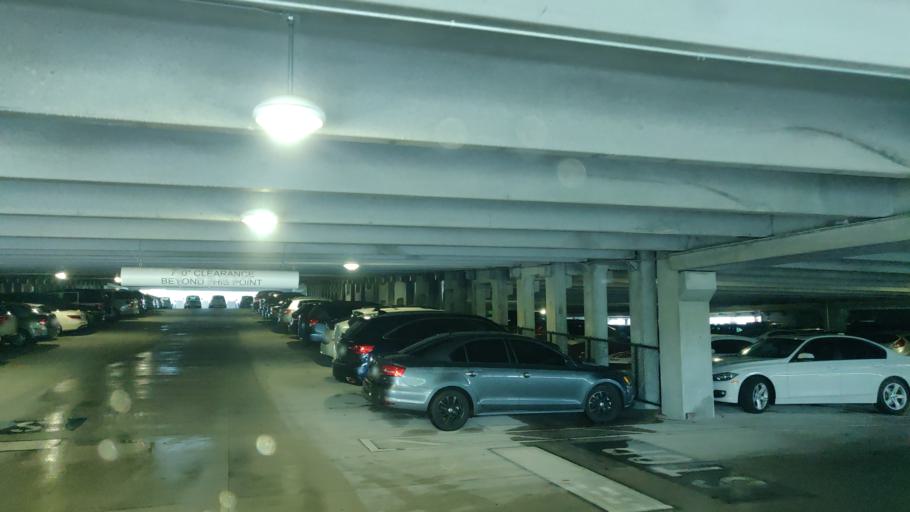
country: US
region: Florida
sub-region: Pinellas County
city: Safety Harbor
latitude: 27.9641
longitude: -82.6989
